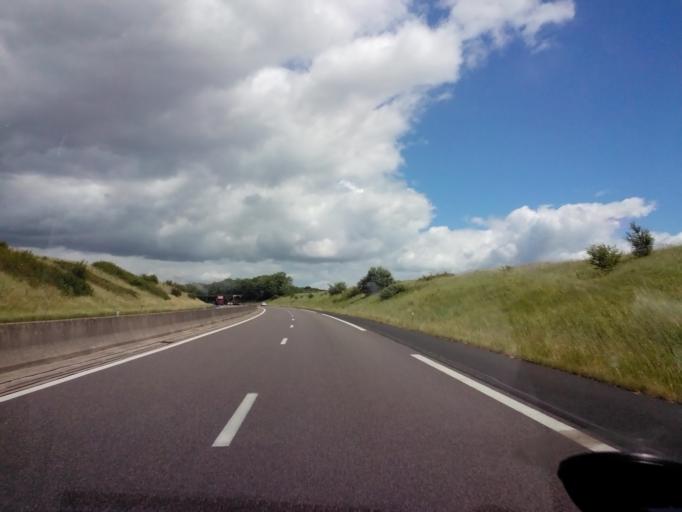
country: FR
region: Lorraine
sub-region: Departement des Vosges
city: Bulgneville
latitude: 48.2272
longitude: 5.8555
